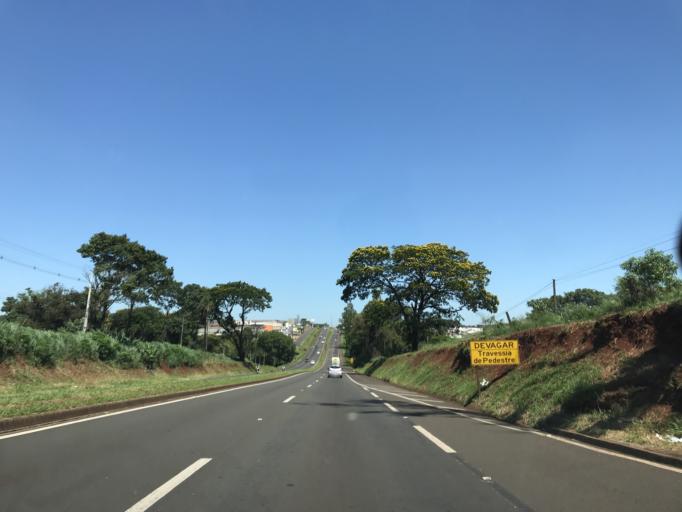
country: BR
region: Parana
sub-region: Sarandi
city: Sarandi
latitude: -23.4549
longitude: -51.8478
